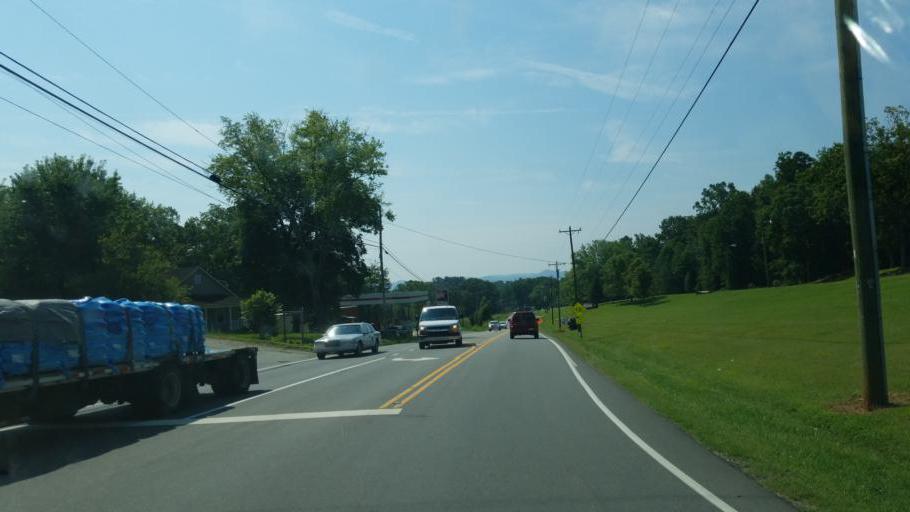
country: US
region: North Carolina
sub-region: Burke County
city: Glen Alpine
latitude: 35.7778
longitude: -81.7558
